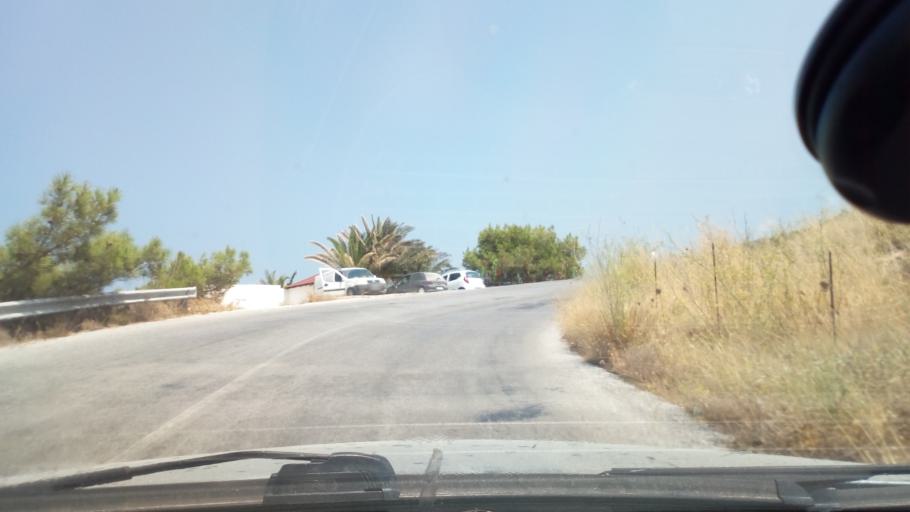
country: GR
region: North Aegean
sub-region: Nomos Samou
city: Agios Kirykos
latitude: 37.6347
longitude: 26.1233
